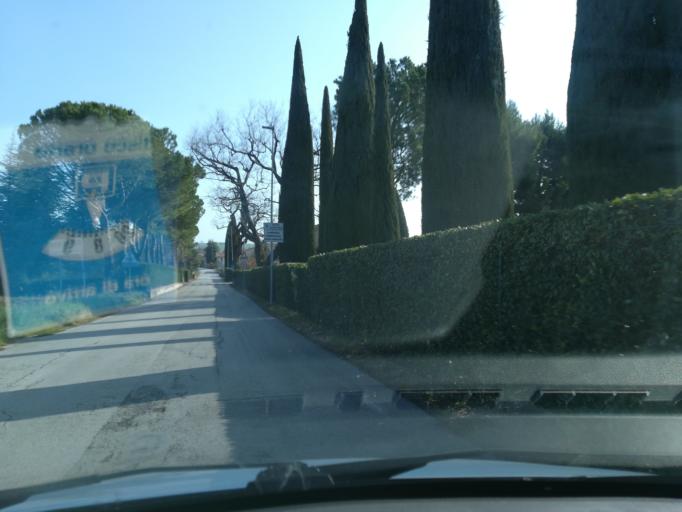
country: IT
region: The Marches
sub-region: Provincia di Macerata
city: Villa Potenza
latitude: 43.3204
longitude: 13.4391
